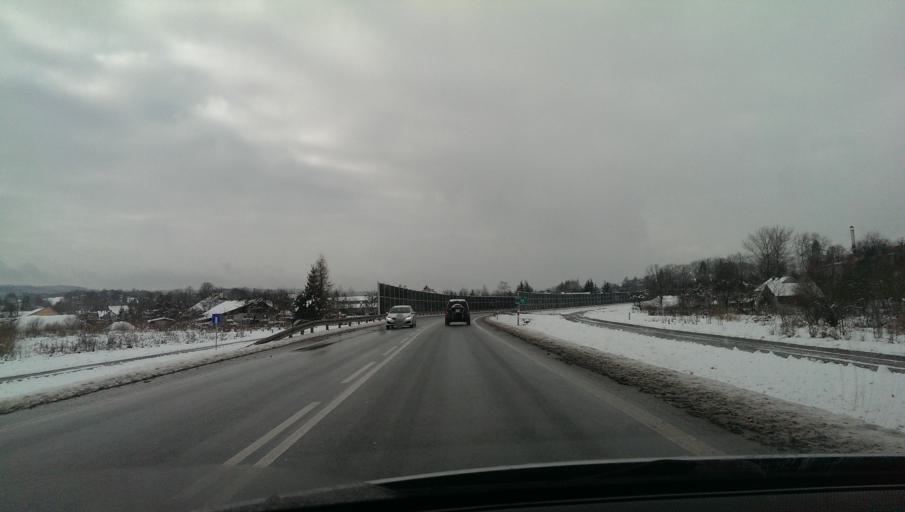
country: PL
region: Subcarpathian Voivodeship
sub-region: Powiat brzozowski
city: Brzozow
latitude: 49.7035
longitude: 22.0277
